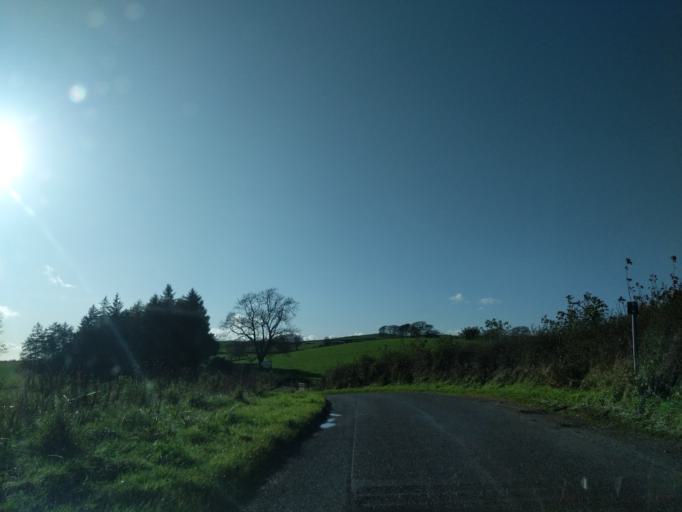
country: GB
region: Scotland
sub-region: Dumfries and Galloway
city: Dalbeattie
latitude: 55.0426
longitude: -3.7439
